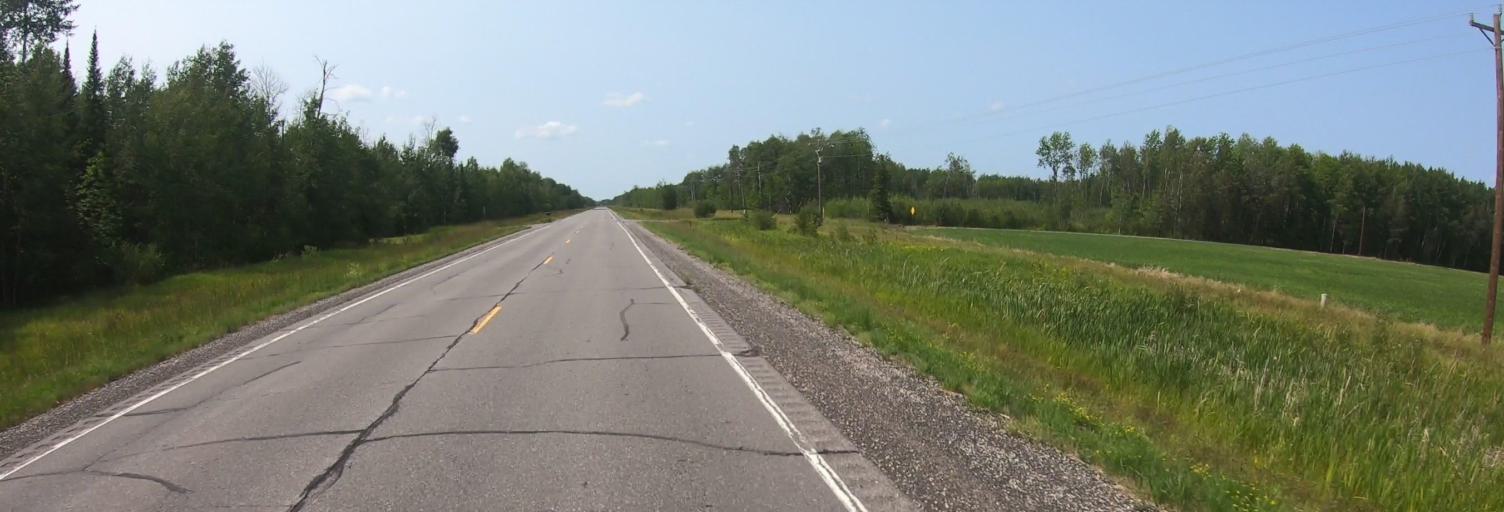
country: US
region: Minnesota
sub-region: Lake of the Woods County
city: Baudette
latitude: 48.6996
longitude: -94.3850
